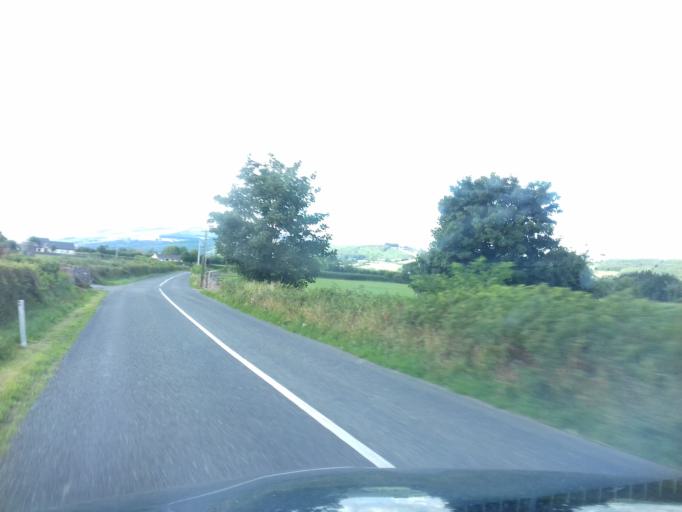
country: IE
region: Munster
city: Carrick-on-Suir
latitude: 52.3839
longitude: -7.4613
